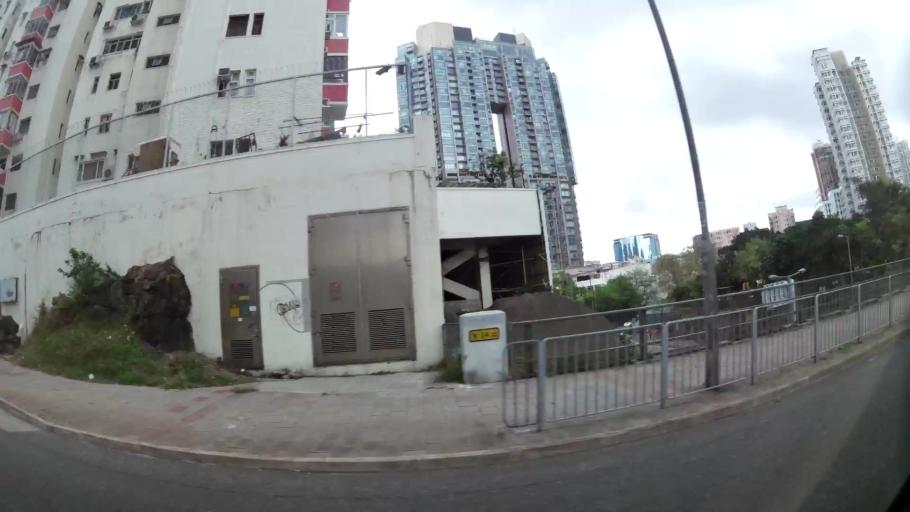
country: HK
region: Kowloon City
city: Kowloon
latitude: 22.3101
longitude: 114.1846
